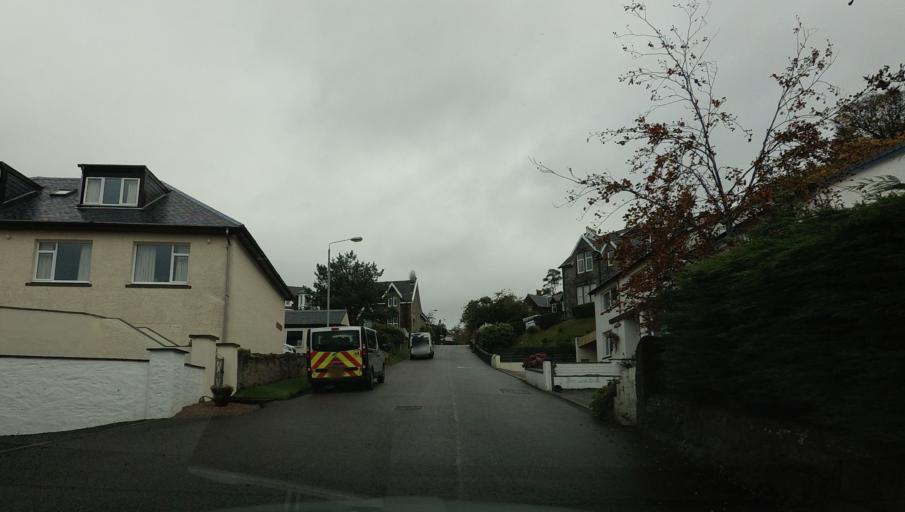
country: GB
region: Scotland
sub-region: Argyll and Bute
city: Oban
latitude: 56.4143
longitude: -5.4681
